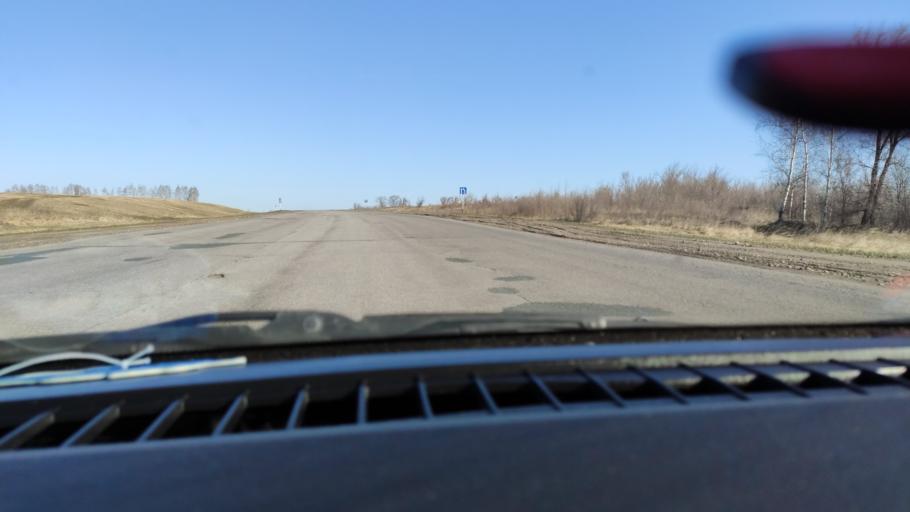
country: RU
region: Samara
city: Varlamovo
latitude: 53.1074
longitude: 48.3564
